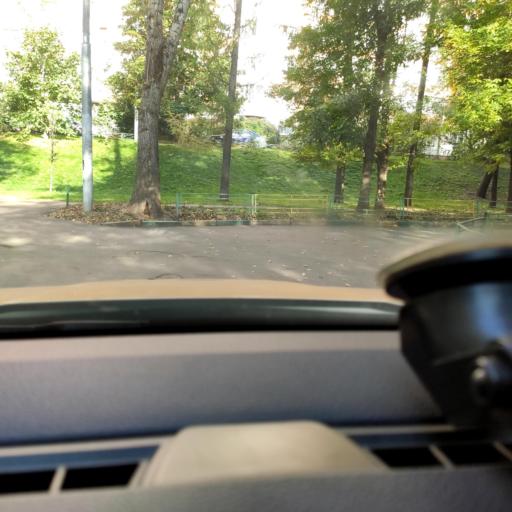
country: RU
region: Moscow
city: Golovinskiy
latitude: 55.8569
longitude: 37.5029
